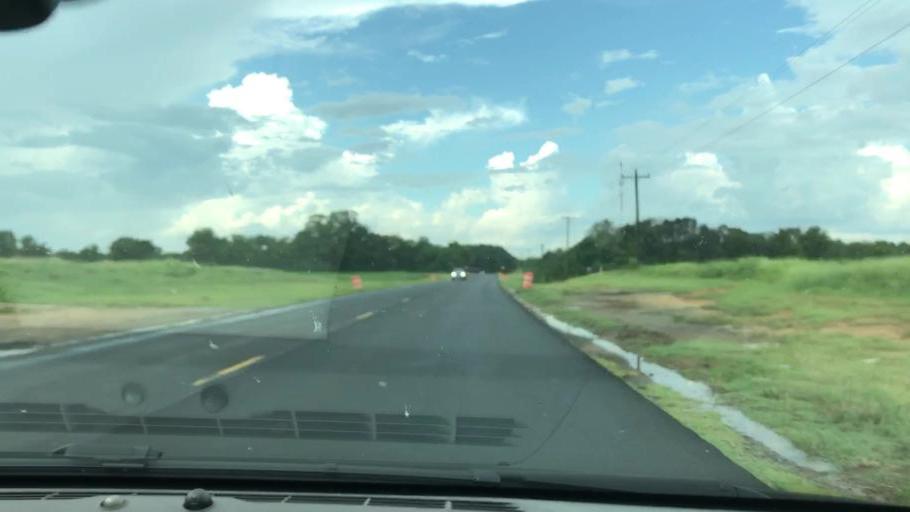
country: US
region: Georgia
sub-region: Early County
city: Blakely
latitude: 31.3974
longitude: -84.9536
